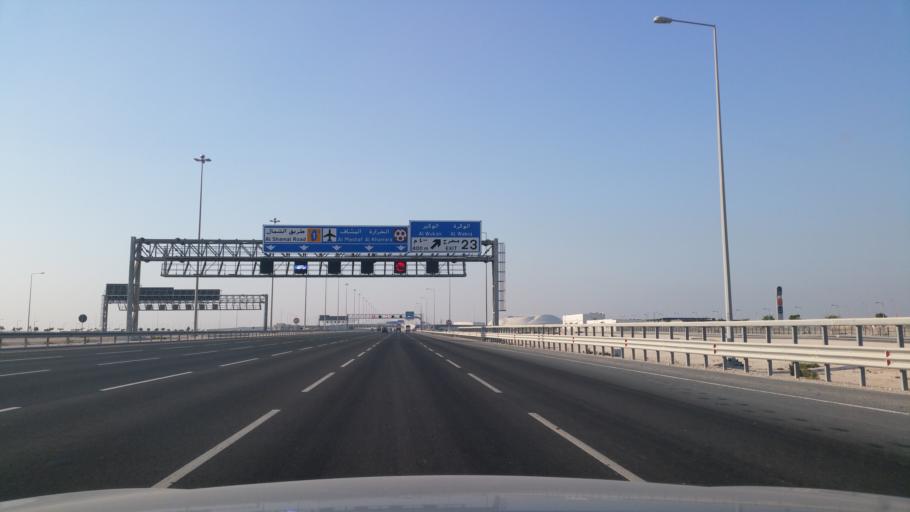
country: QA
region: Al Wakrah
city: Al Wakrah
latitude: 25.1428
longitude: 51.5799
